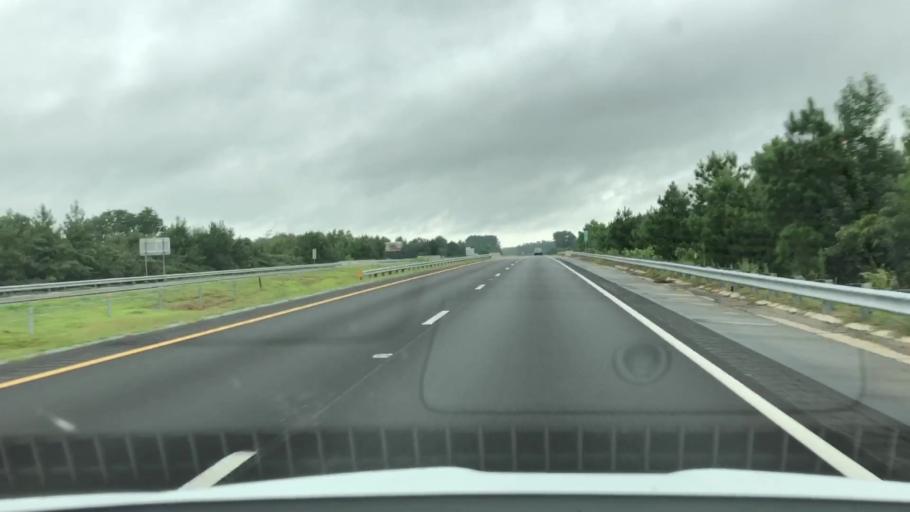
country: US
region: North Carolina
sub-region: Wayne County
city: Goldsboro
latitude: 35.4412
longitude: -77.9843
